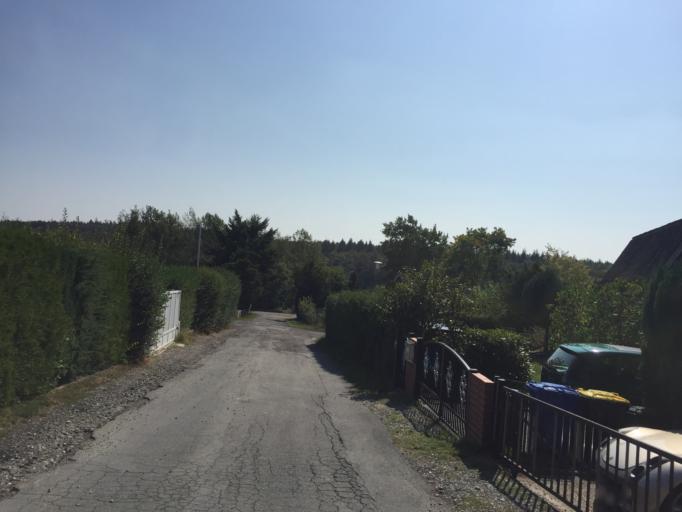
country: DE
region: Hesse
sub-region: Regierungsbezirk Darmstadt
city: Butzbach
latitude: 50.4213
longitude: 8.5904
